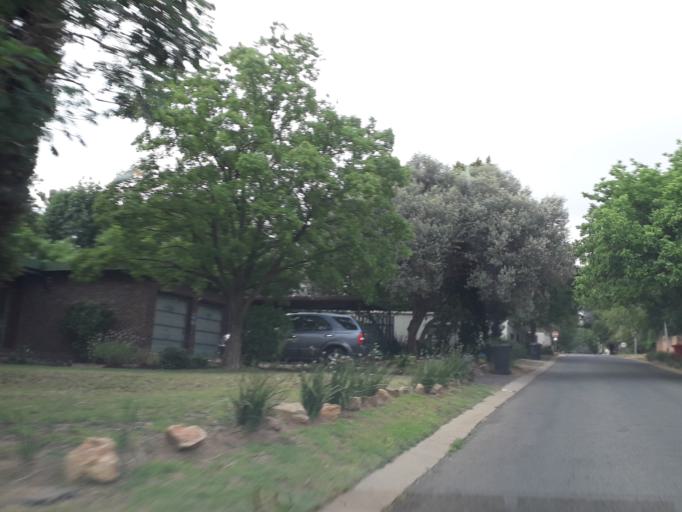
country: ZA
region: Gauteng
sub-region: City of Johannesburg Metropolitan Municipality
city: Roodepoort
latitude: -26.1034
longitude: 27.9709
